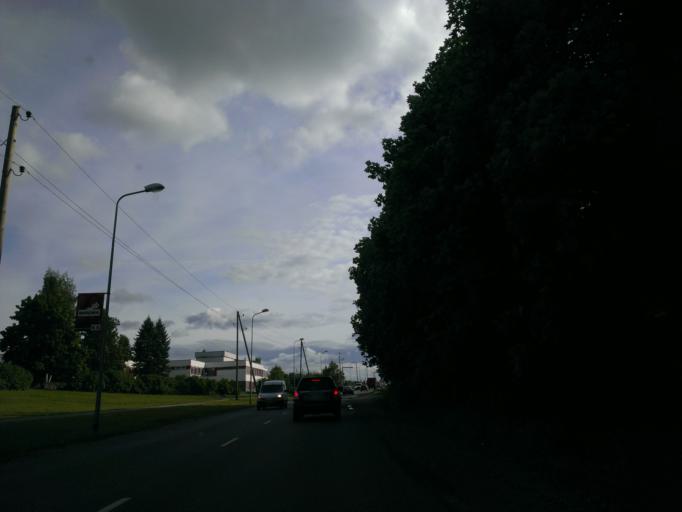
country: LV
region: Stopini
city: Ulbroka
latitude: 56.9605
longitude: 24.2528
